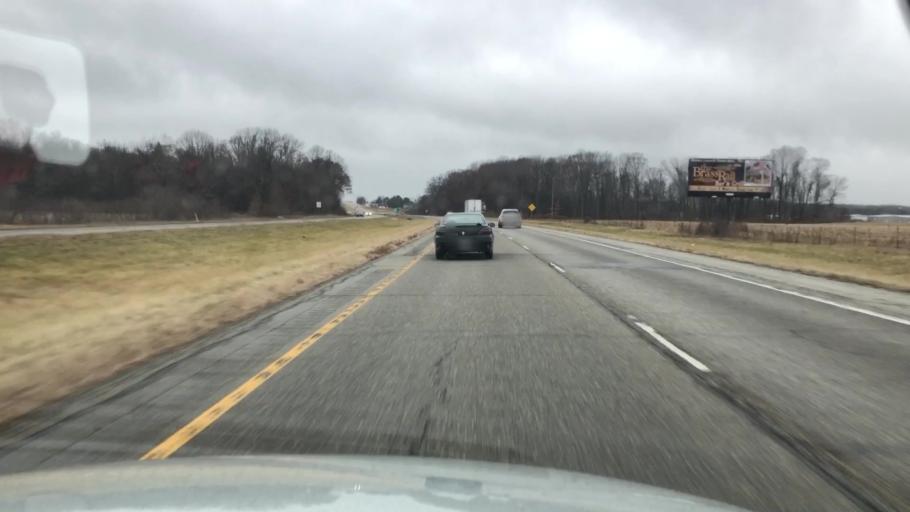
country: US
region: Indiana
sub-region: Marshall County
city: Plymouth
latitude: 41.3622
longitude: -86.2994
